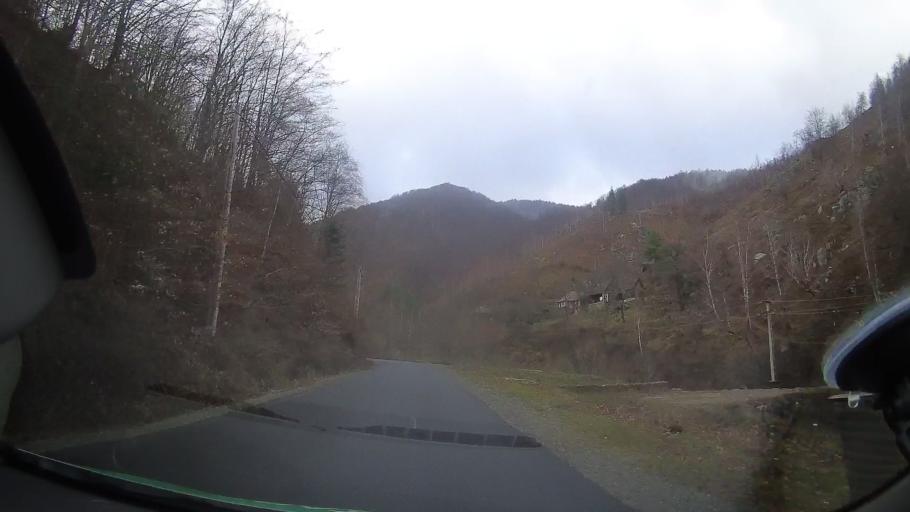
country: RO
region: Cluj
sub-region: Comuna Valea Ierii
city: Valea Ierii
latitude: 46.6430
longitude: 23.3237
